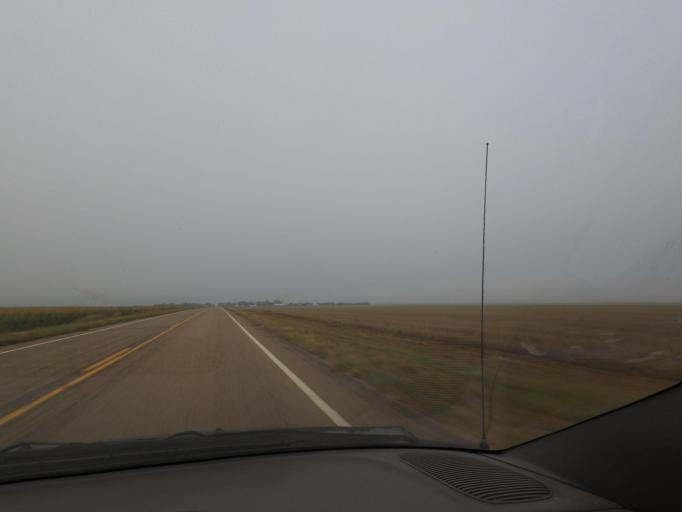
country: US
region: Colorado
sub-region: Yuma County
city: Wray
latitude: 39.7026
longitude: -102.2795
